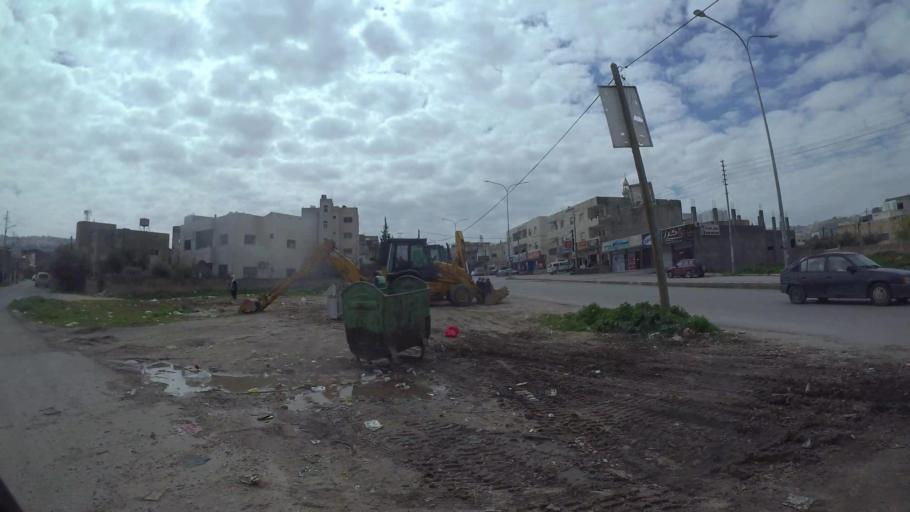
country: JO
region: Amman
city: Al Jubayhah
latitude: 32.0633
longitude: 35.8271
